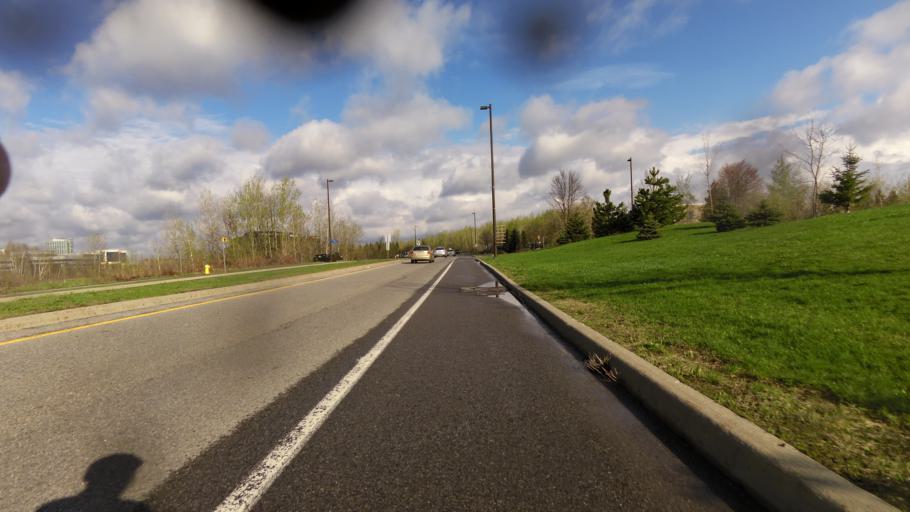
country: CA
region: Ontario
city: Bells Corners
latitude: 45.3472
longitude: -75.9025
